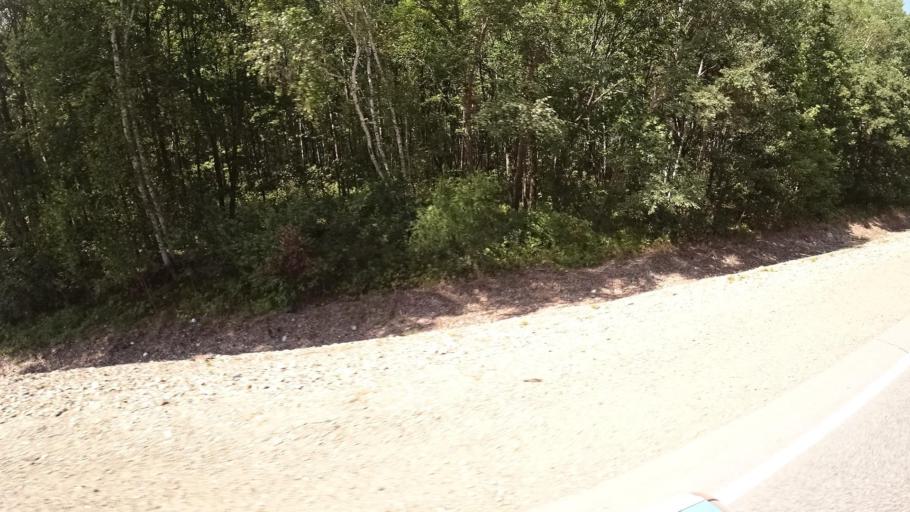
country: RU
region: Khabarovsk Krai
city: Khor
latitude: 47.9796
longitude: 135.0858
